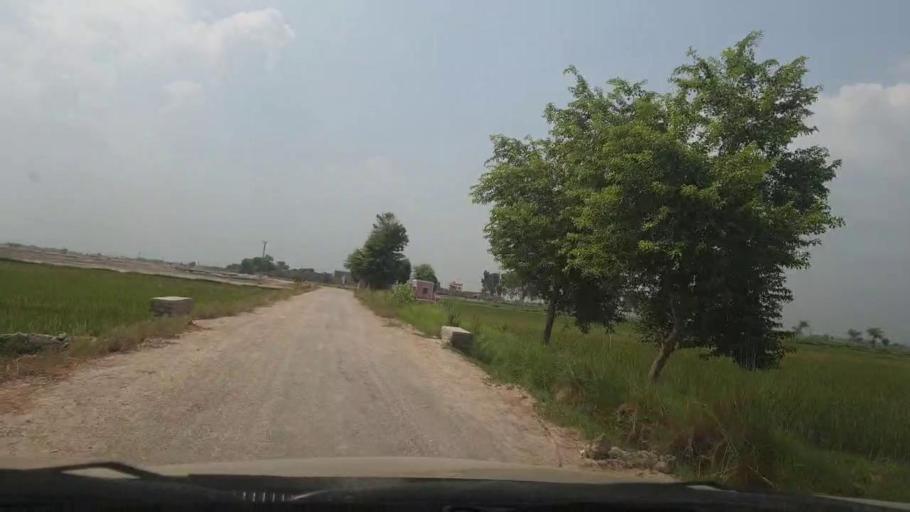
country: PK
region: Sindh
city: Naudero
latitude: 27.6952
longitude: 68.2577
